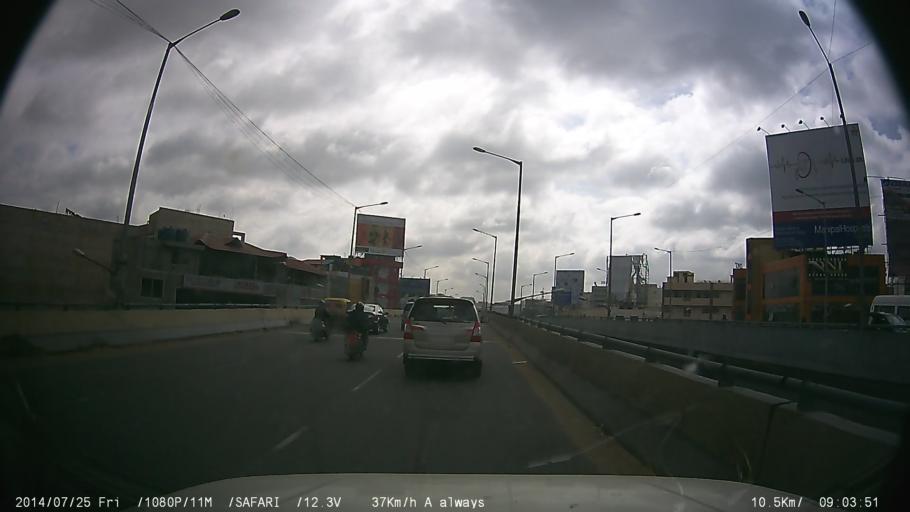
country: IN
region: Karnataka
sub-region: Bangalore Urban
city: Bangalore
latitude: 12.9259
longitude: 77.6762
